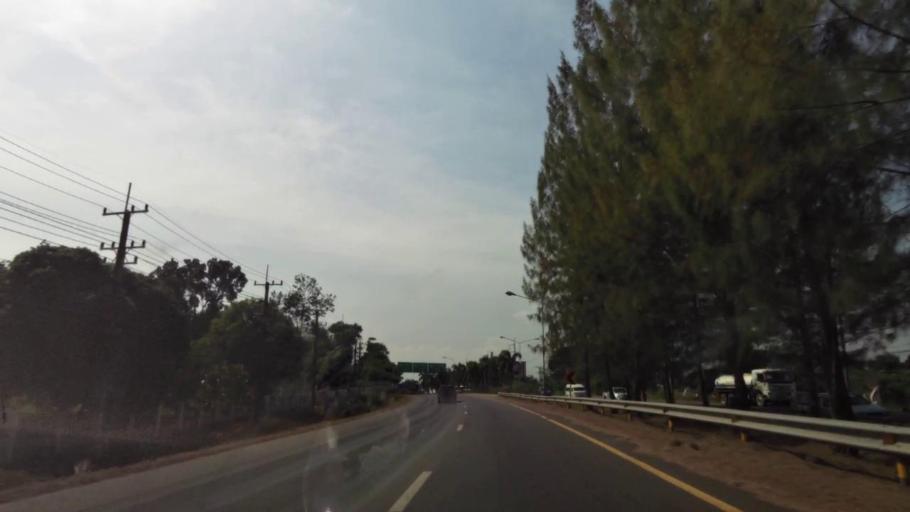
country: TH
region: Chanthaburi
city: Chanthaburi
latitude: 12.6668
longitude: 102.0955
